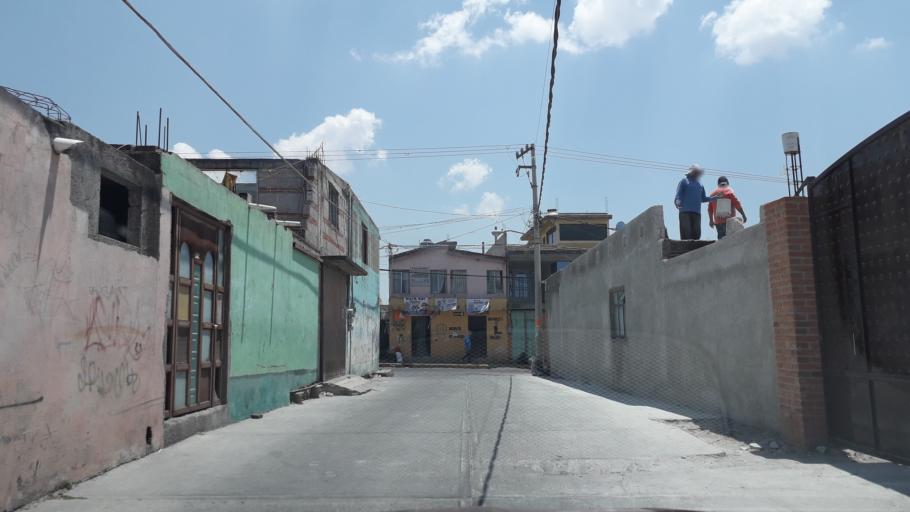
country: MX
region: Puebla
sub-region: Puebla
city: Santa Maria Xonacatepec
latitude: 19.0848
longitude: -98.1064
